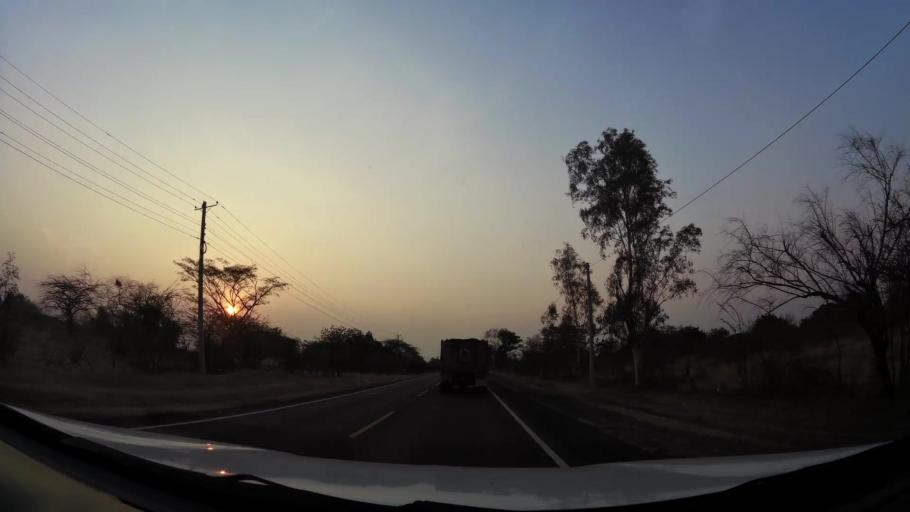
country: NI
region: Leon
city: La Paz Centro
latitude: 12.3064
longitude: -86.7790
